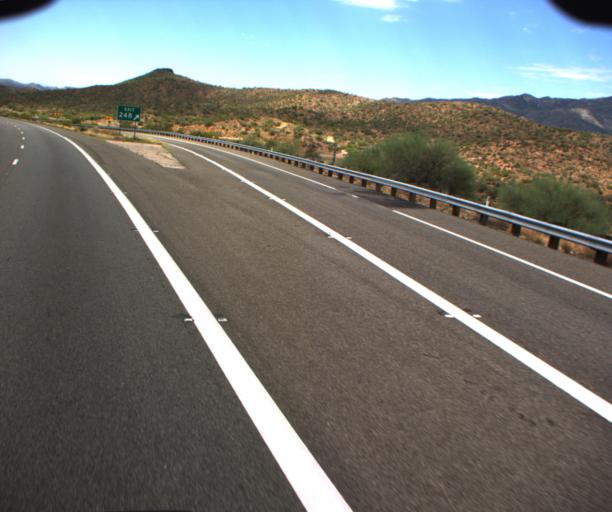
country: US
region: Arizona
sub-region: Yavapai County
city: Black Canyon City
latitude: 34.1491
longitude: -112.1495
